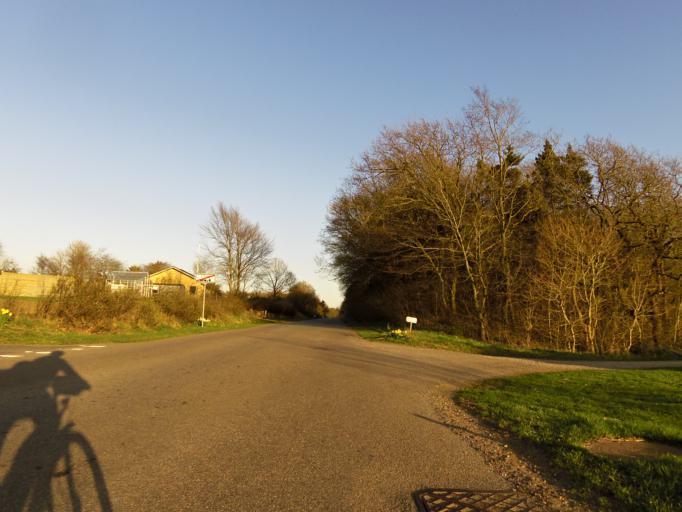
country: DK
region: Central Jutland
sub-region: Holstebro Kommune
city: Vinderup
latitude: 56.5203
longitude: 8.7883
